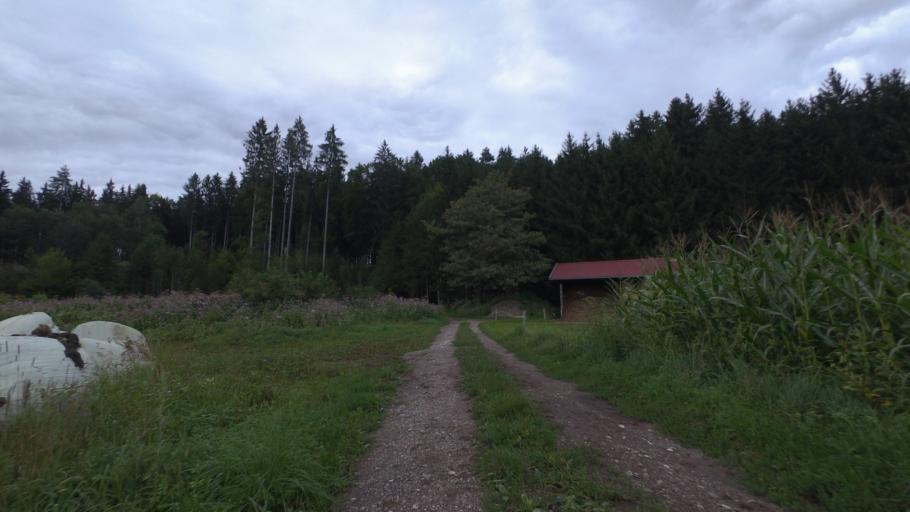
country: DE
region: Bavaria
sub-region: Upper Bavaria
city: Nussdorf
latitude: 47.8910
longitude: 12.5770
